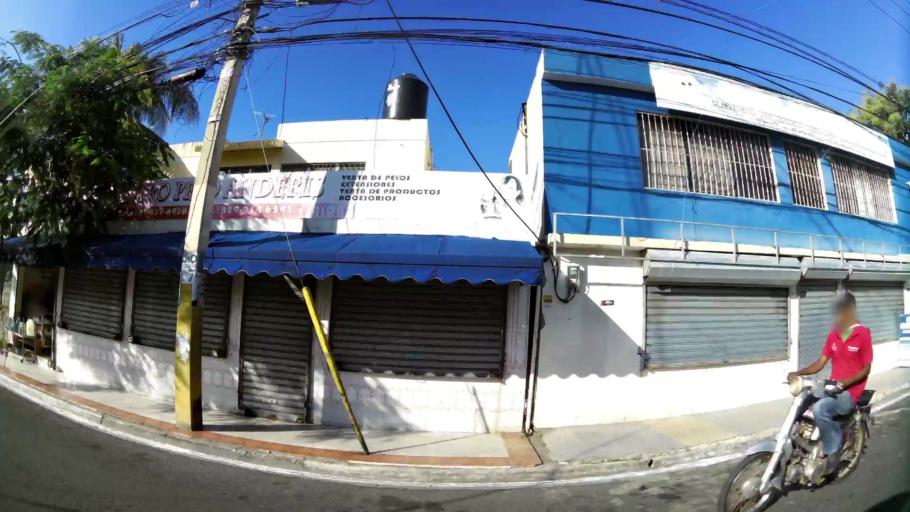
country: DO
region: Santo Domingo
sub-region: Santo Domingo
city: Santo Domingo Este
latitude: 18.4724
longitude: -69.8510
